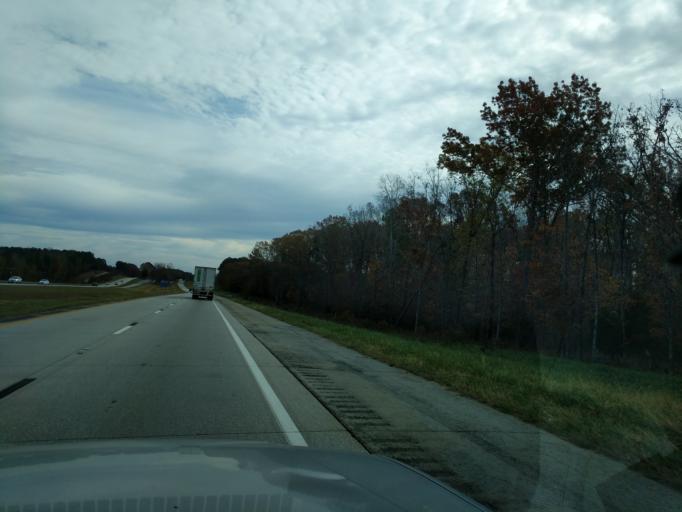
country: US
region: South Carolina
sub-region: Laurens County
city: Watts Mills
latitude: 34.5454
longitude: -81.9786
